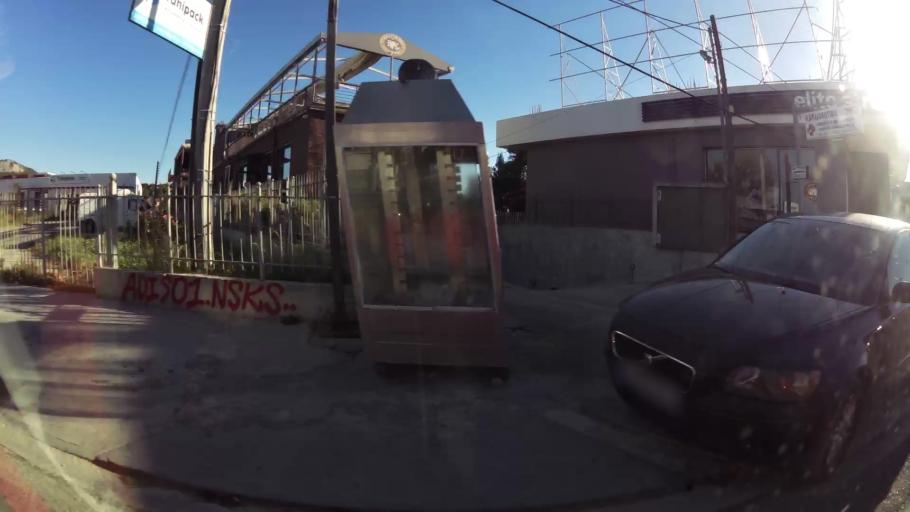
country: GR
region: Attica
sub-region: Nomarchia Anatolikis Attikis
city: Pikermi
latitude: 38.0038
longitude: 23.9469
